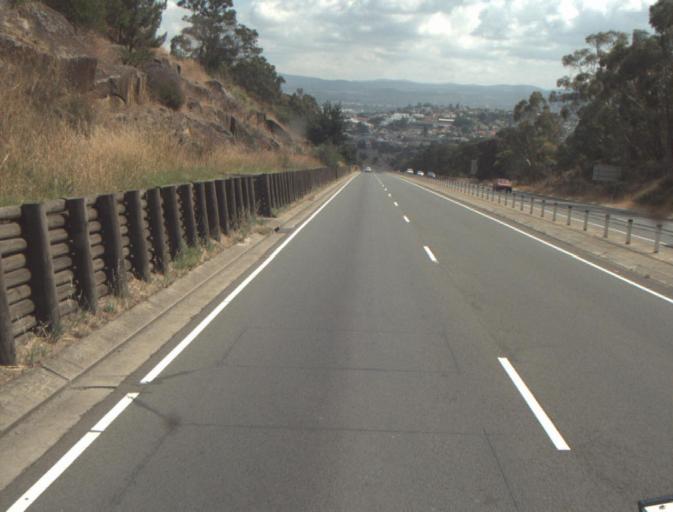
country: AU
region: Tasmania
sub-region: Launceston
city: Summerhill
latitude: -41.4646
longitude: 147.1427
